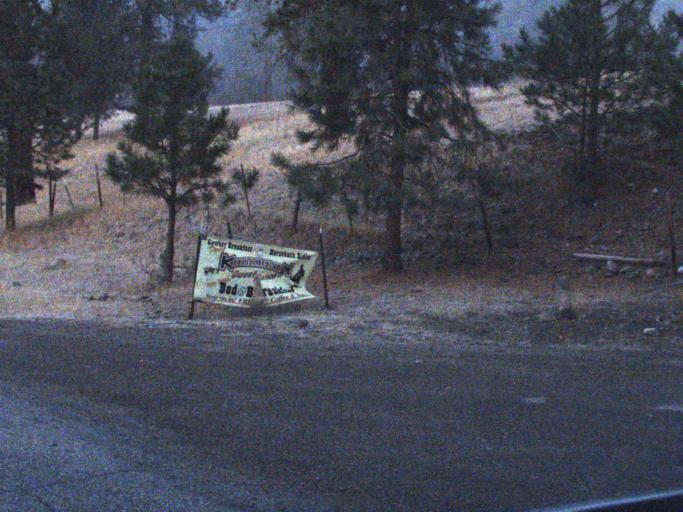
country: US
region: Washington
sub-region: Ferry County
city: Republic
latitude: 48.5912
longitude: -118.7420
